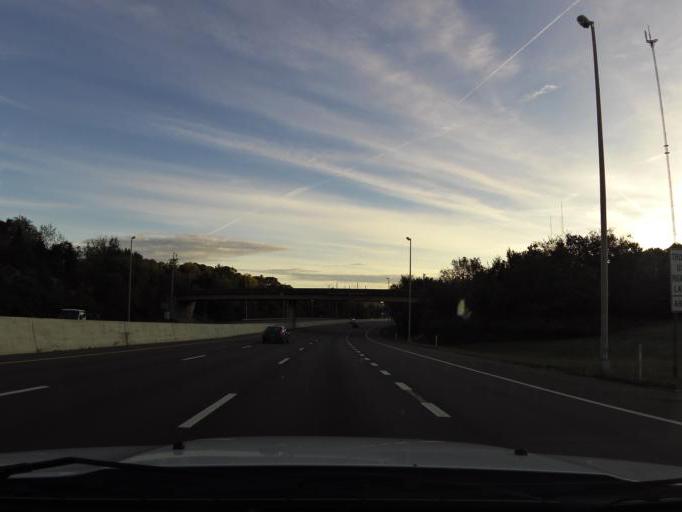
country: US
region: Tennessee
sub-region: Knox County
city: Knoxville
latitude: 35.9930
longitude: -83.9669
